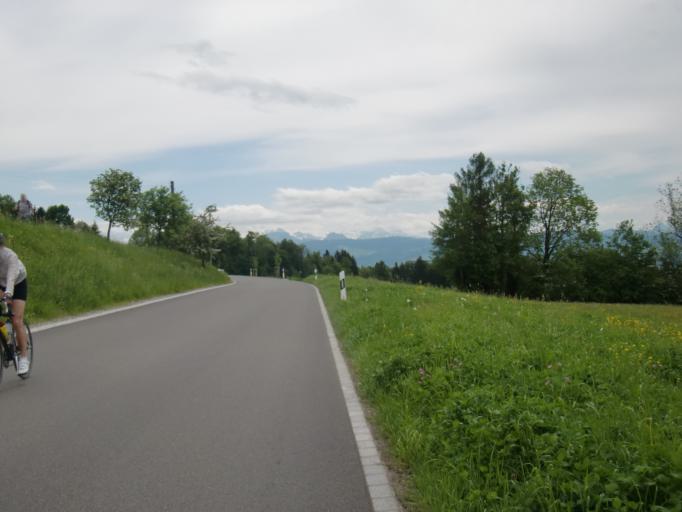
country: CH
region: Zurich
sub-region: Bezirk Hinwil
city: Hadlikon
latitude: 47.2941
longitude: 8.8695
